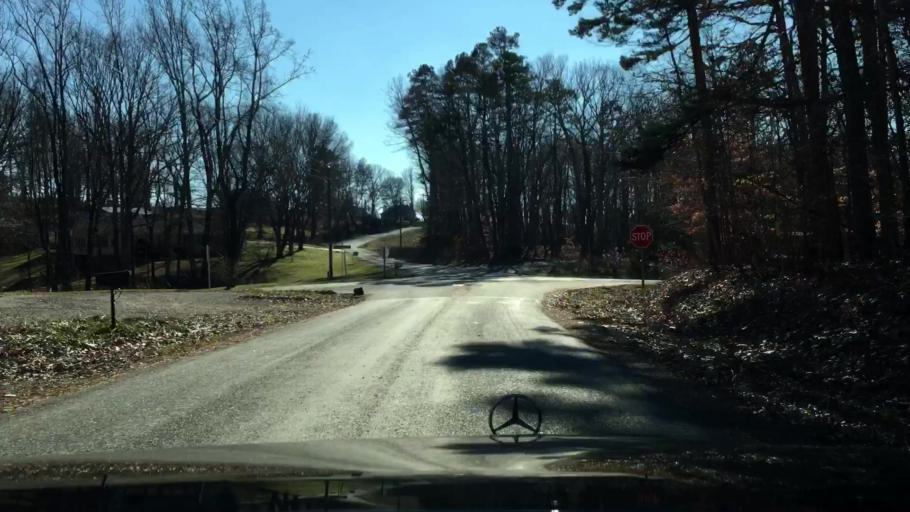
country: US
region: Virginia
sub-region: Pittsylvania County
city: Motley
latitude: 37.1547
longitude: -79.3646
